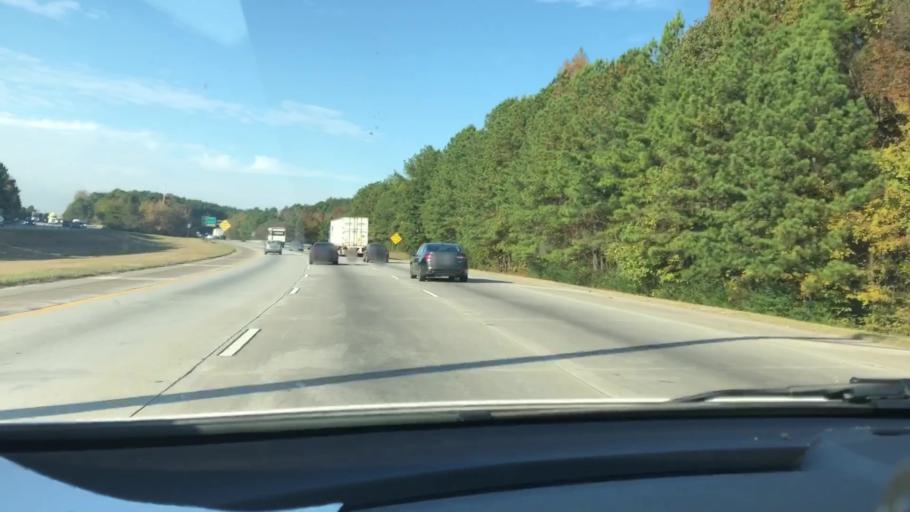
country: US
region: Georgia
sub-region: Clayton County
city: Conley
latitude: 33.6646
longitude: -84.3244
